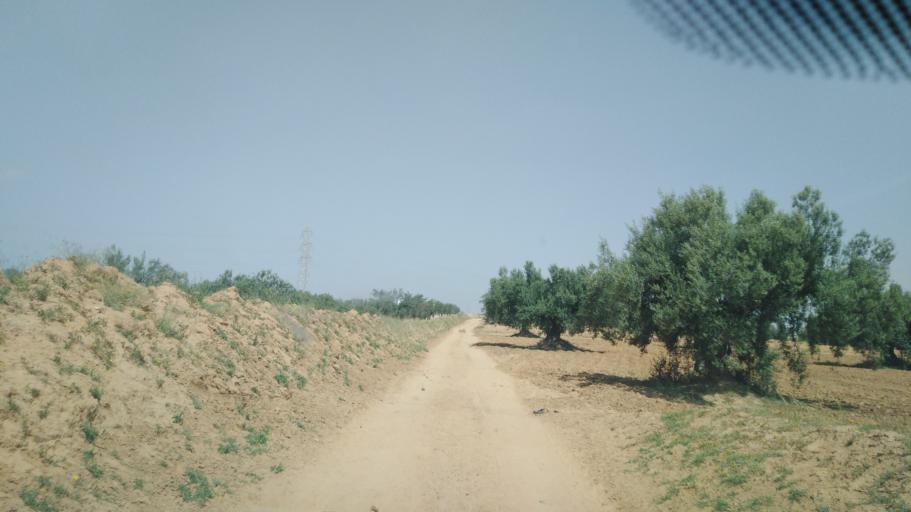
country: TN
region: Safaqis
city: Sfax
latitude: 34.7384
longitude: 10.5725
